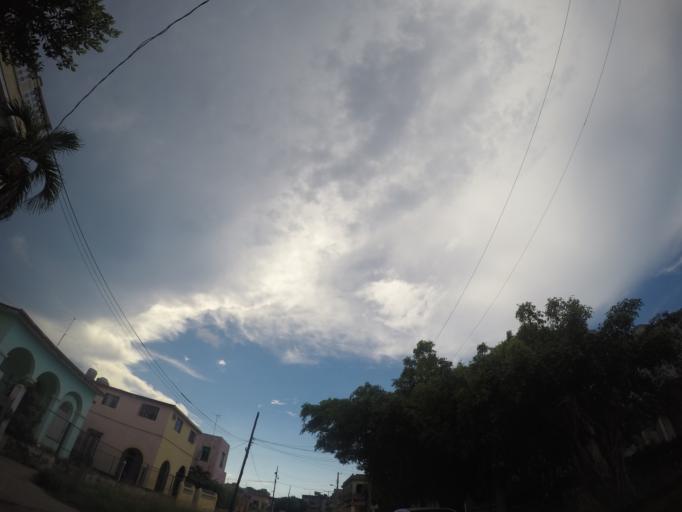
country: CU
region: La Habana
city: Havana
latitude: 23.1164
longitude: -82.4211
